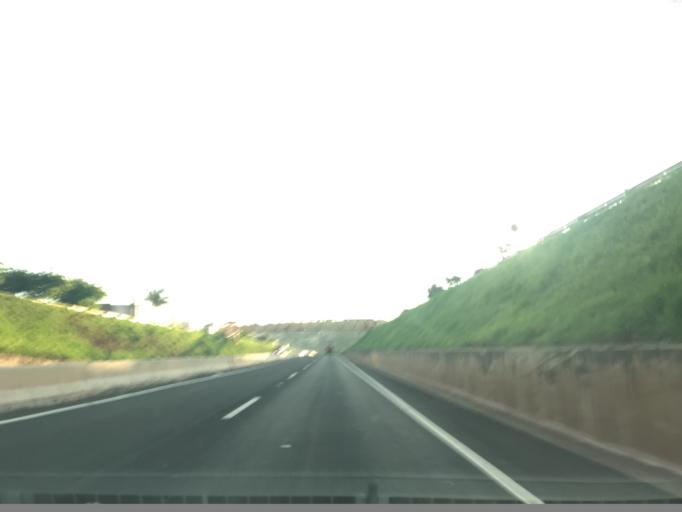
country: BR
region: Parana
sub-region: Maringa
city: Maringa
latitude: -23.3802
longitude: -51.9561
